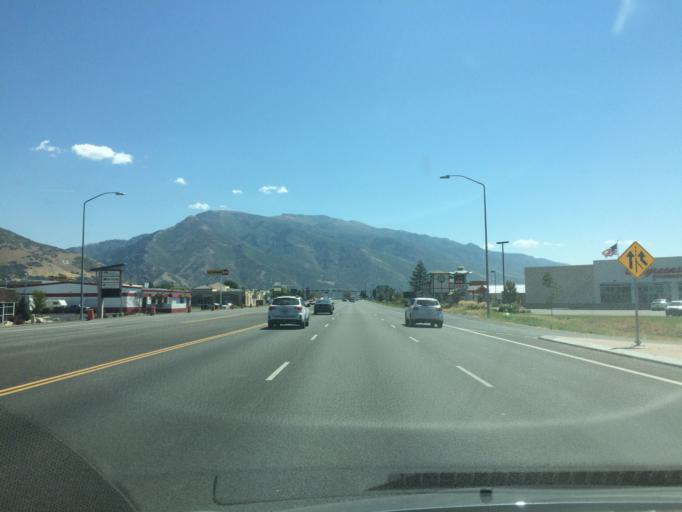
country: US
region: Utah
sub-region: Weber County
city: Uintah
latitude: 41.1547
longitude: -111.9395
